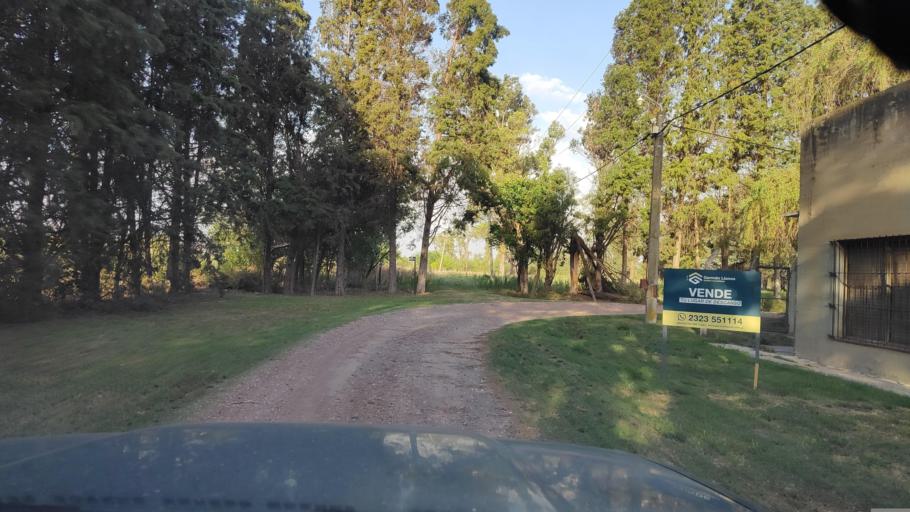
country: AR
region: Buenos Aires
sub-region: Partido de Lujan
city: Lujan
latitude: -34.5474
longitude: -59.1903
